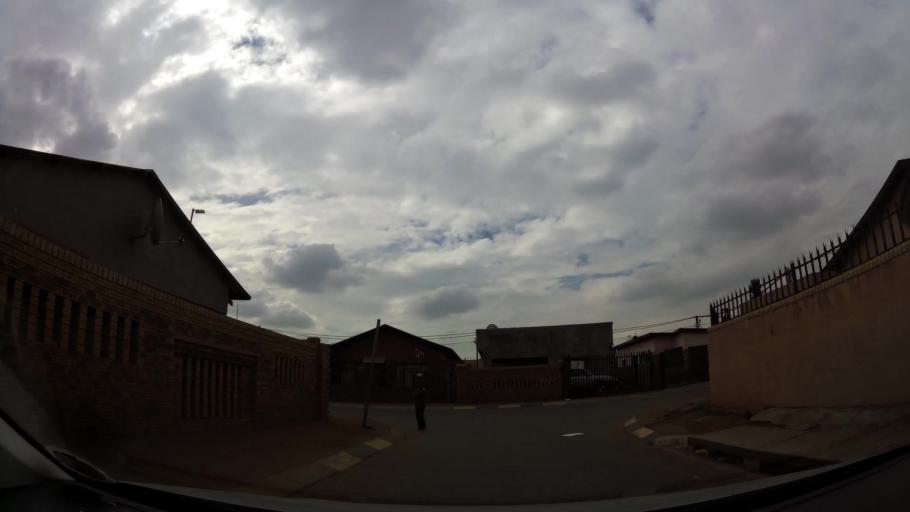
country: ZA
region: Gauteng
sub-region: City of Johannesburg Metropolitan Municipality
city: Soweto
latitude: -26.2732
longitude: 27.8562
